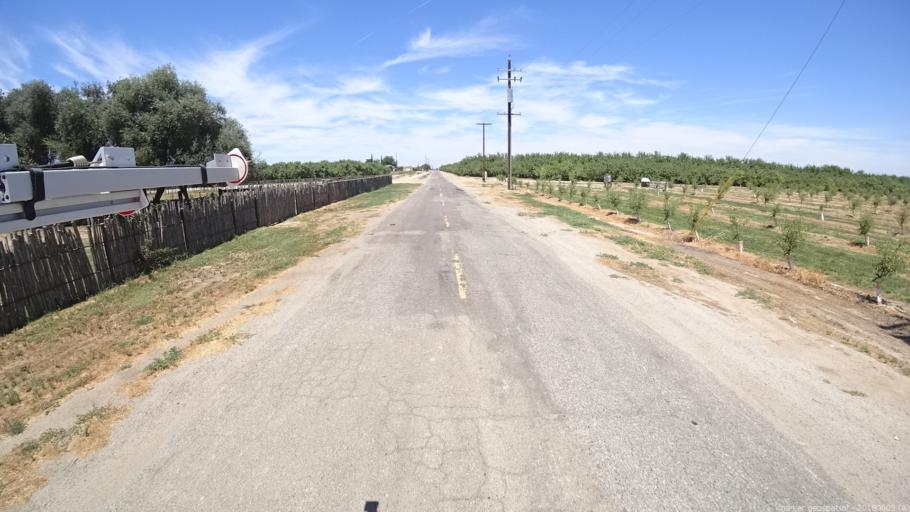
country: US
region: California
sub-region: Madera County
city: Chowchilla
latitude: 37.0977
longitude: -120.2927
